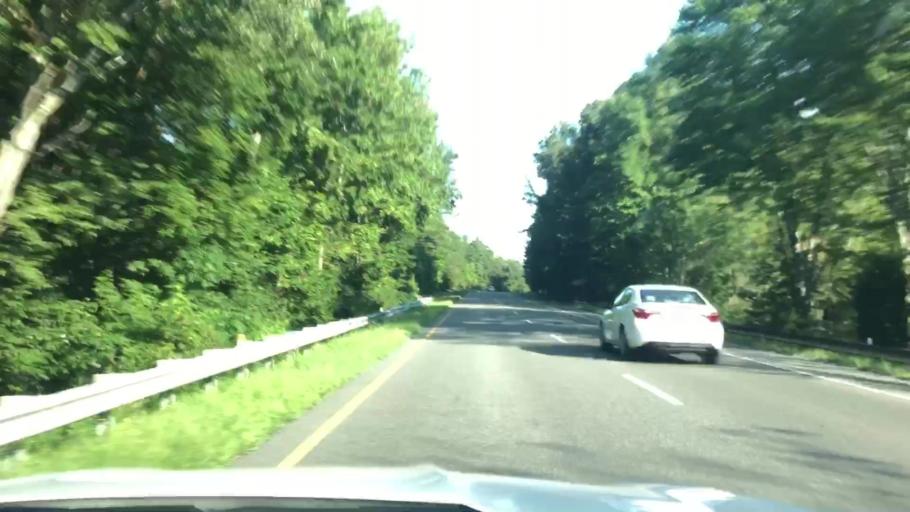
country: US
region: Virginia
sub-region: King and Queen County
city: King and Queen Court House
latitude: 37.7865
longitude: -76.7646
